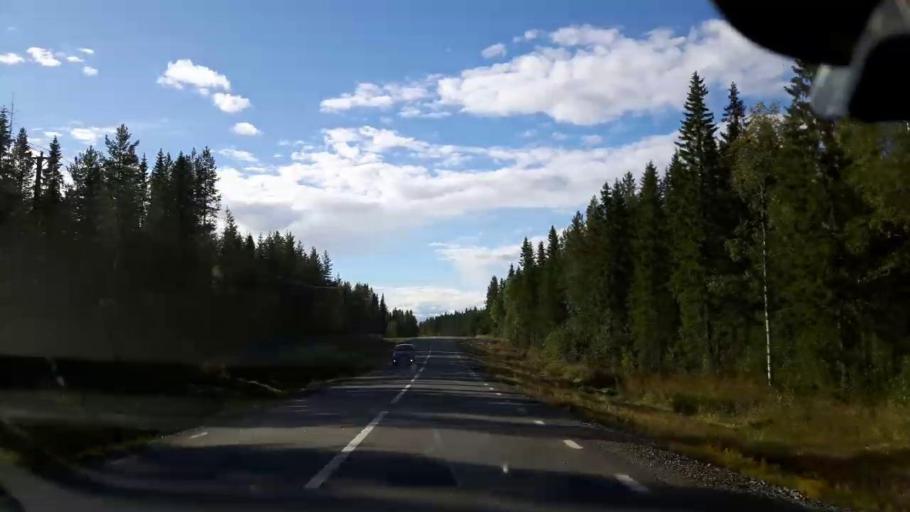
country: SE
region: Jaemtland
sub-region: Stroemsunds Kommun
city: Stroemsund
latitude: 63.5459
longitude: 15.9064
